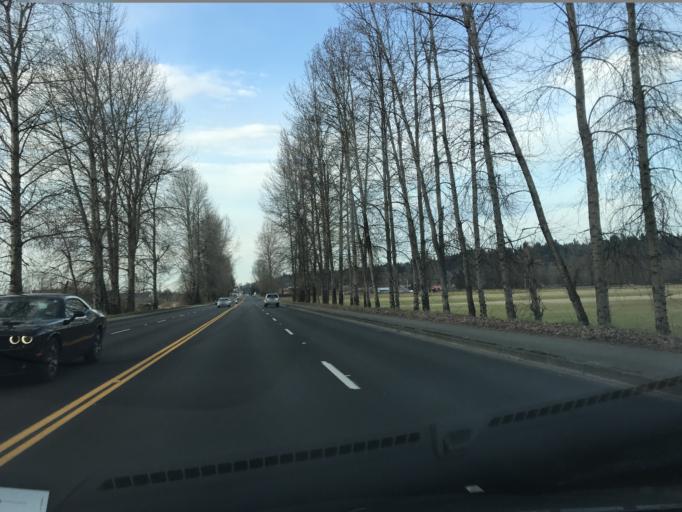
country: US
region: Washington
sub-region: King County
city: Kent
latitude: 47.3562
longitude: -122.2298
